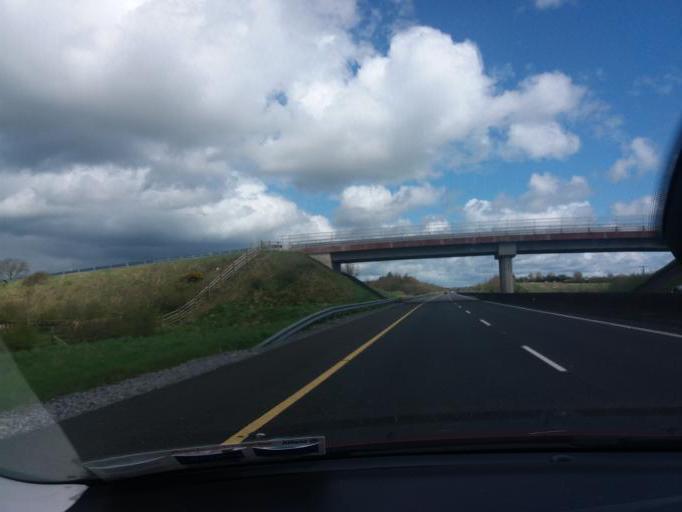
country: IE
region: Leinster
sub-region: Laois
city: Rathdowney
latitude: 52.7892
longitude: -7.5229
